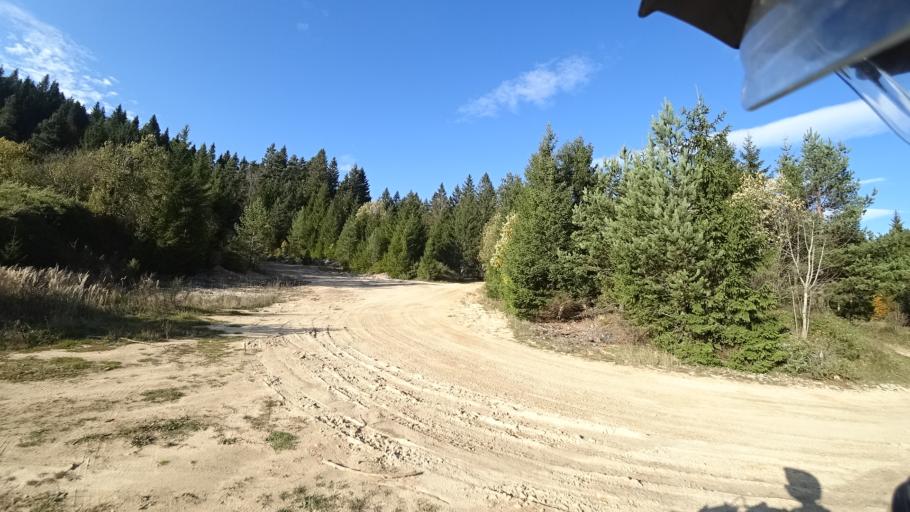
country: HR
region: Licko-Senjska
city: Jezerce
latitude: 44.9280
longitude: 15.4632
